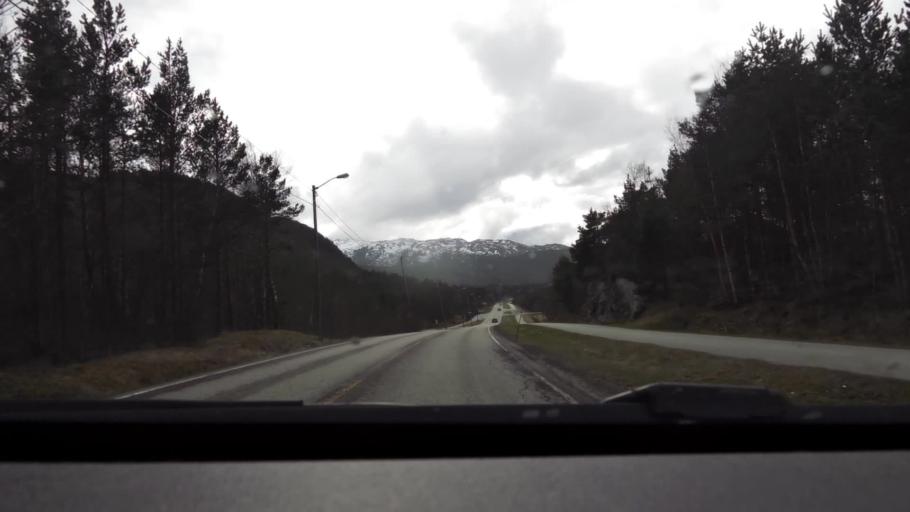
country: NO
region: More og Romsdal
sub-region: Kristiansund
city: Rensvik
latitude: 63.0904
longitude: 7.7948
